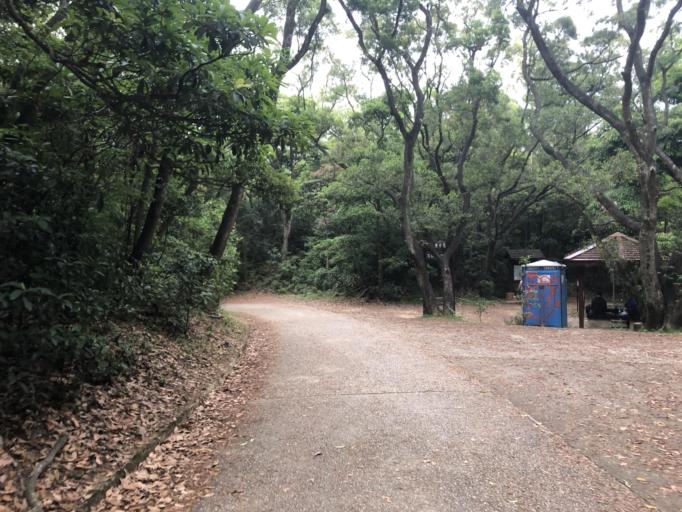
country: HK
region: Sha Tin
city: Sha Tin
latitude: 22.3947
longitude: 114.1681
